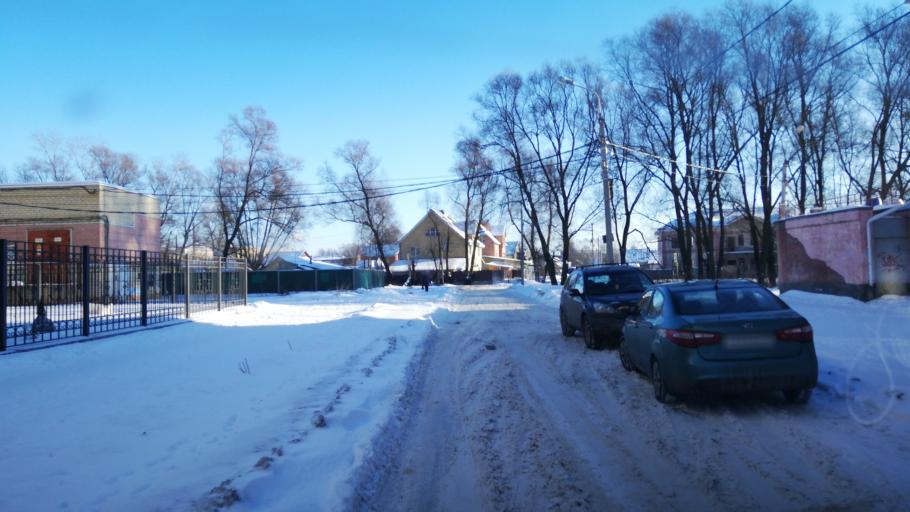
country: RU
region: Jaroslavl
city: Yaroslavl
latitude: 57.6102
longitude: 39.8998
